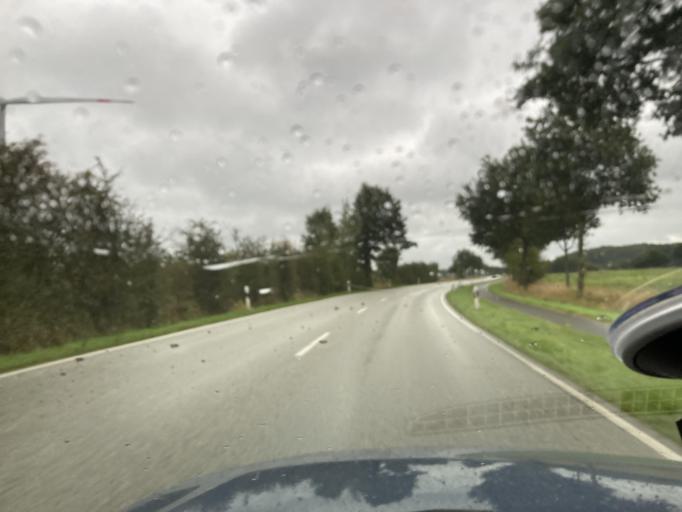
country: DE
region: Schleswig-Holstein
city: Hamdorf
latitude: 54.2394
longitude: 9.5229
